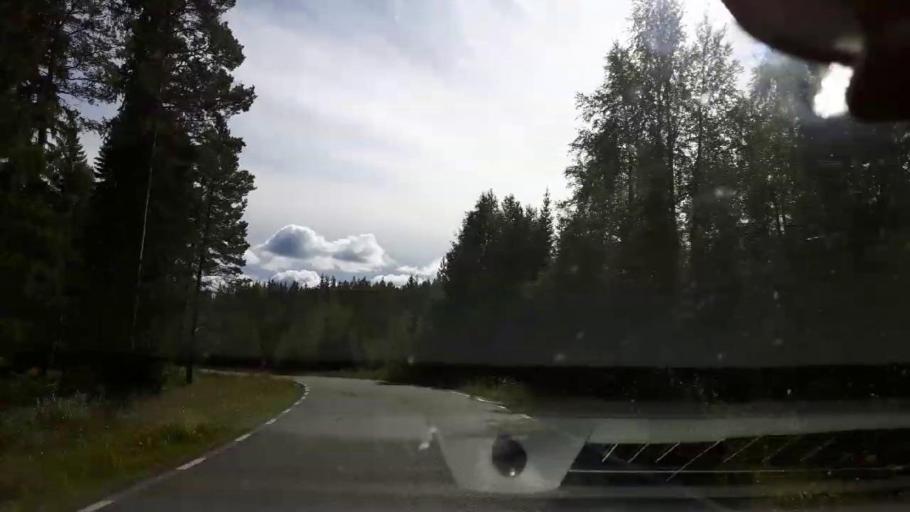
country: SE
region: Jaemtland
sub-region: Braecke Kommun
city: Braecke
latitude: 63.2050
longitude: 15.3544
